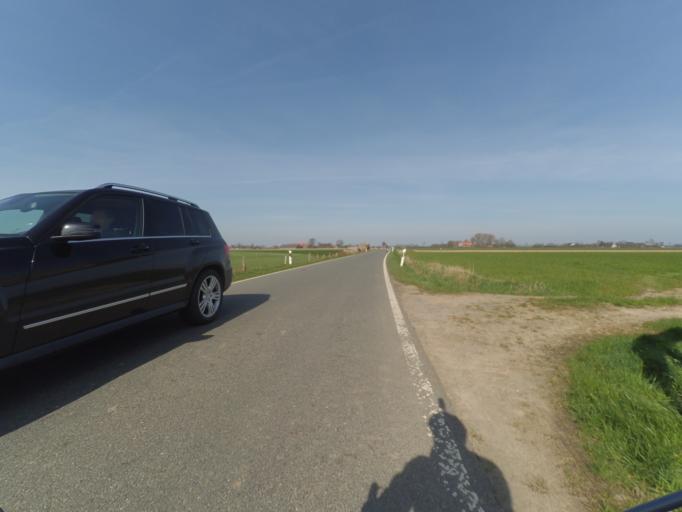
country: DE
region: North Rhine-Westphalia
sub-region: Regierungsbezirk Dusseldorf
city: Kranenburg
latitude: 51.8011
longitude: 6.0737
